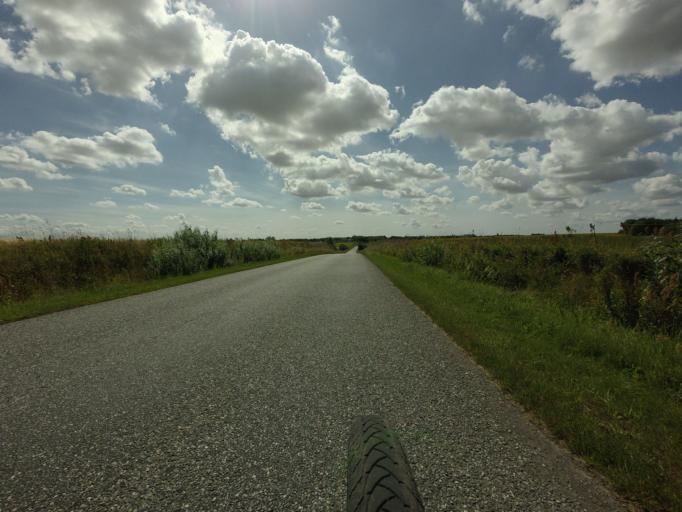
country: DK
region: North Denmark
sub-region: Hjorring Kommune
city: Hjorring
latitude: 57.4696
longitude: 9.9053
